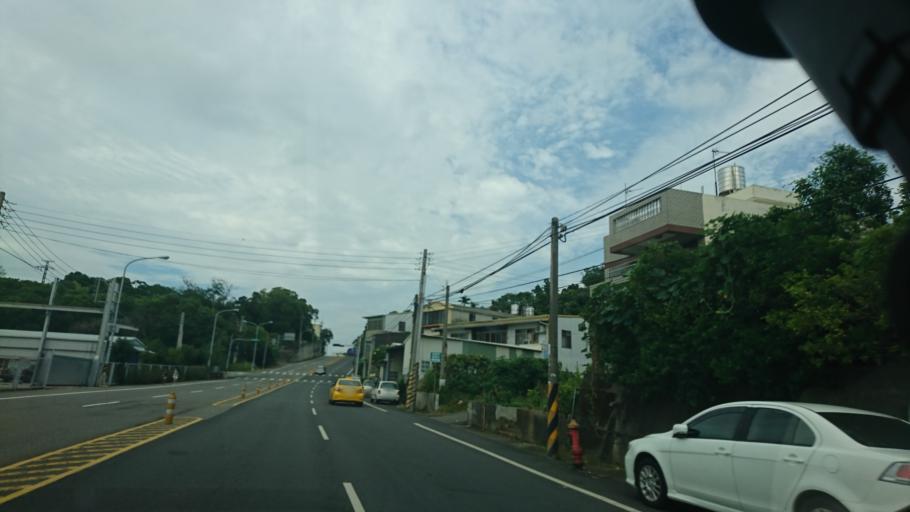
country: TW
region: Taiwan
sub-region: Miaoli
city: Miaoli
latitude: 24.5281
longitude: 120.7989
